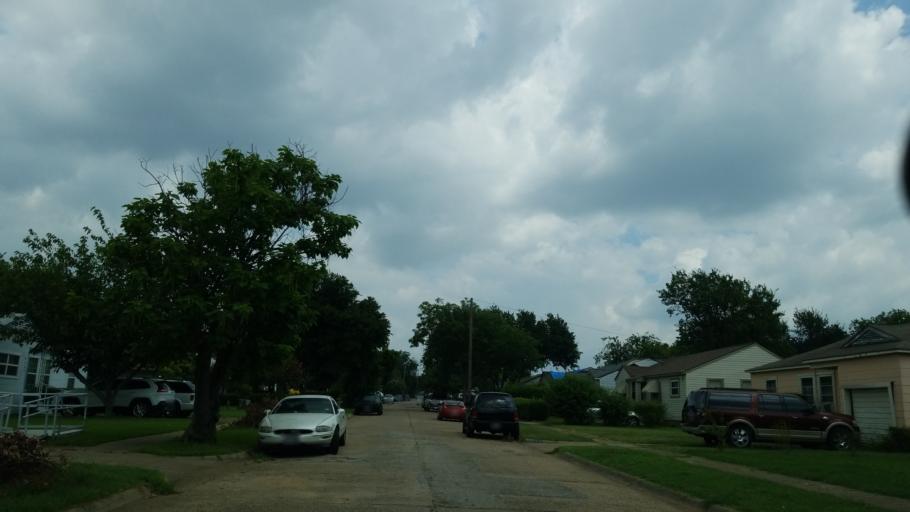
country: US
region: Texas
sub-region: Dallas County
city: University Park
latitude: 32.8503
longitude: -96.8343
